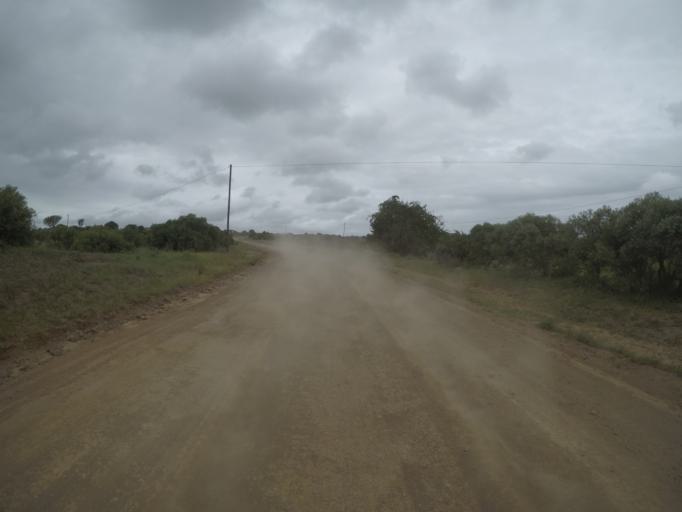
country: ZA
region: KwaZulu-Natal
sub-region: uThungulu District Municipality
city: Empangeni
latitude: -28.5981
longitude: 31.8380
